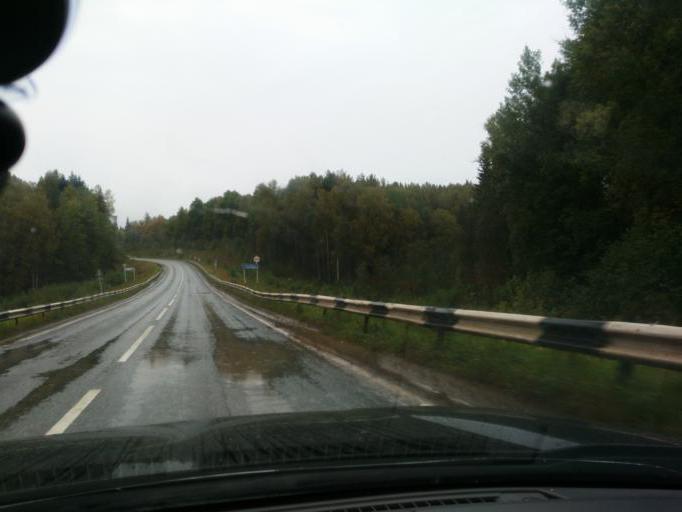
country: RU
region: Perm
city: Yugo-Kamskiy
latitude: 57.5927
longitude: 55.6645
